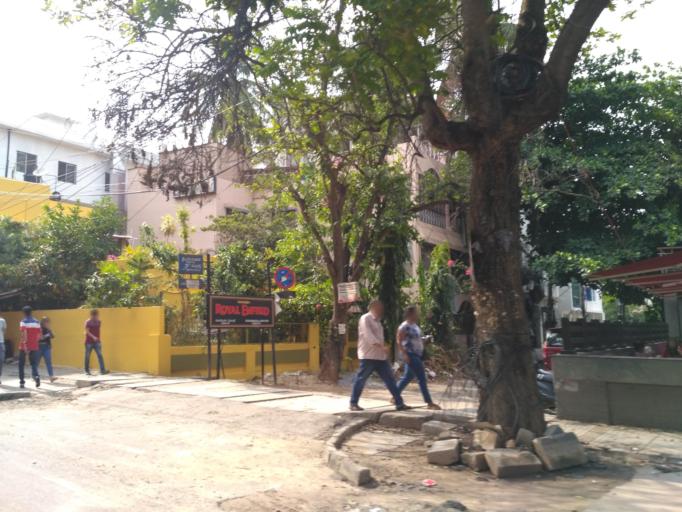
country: IN
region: Karnataka
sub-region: Bangalore Urban
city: Bangalore
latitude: 12.9338
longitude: 77.6174
